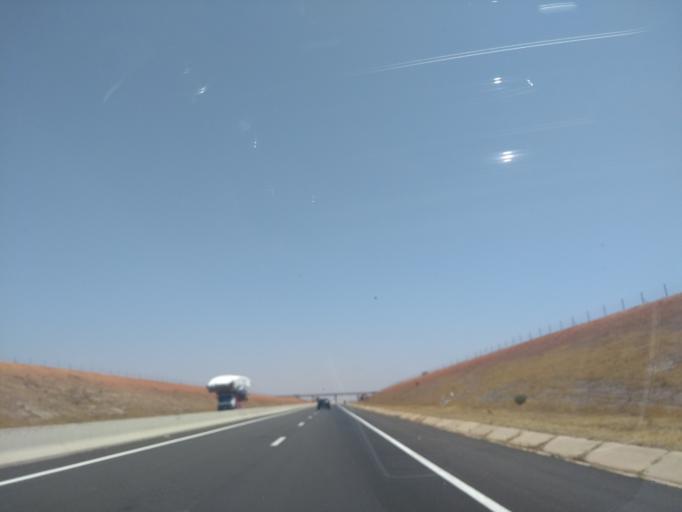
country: MA
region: Marrakech-Tensift-Al Haouz
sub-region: Kelaa-Des-Sraghna
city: Sidi Abdallah
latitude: 32.3160
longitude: -7.9589
